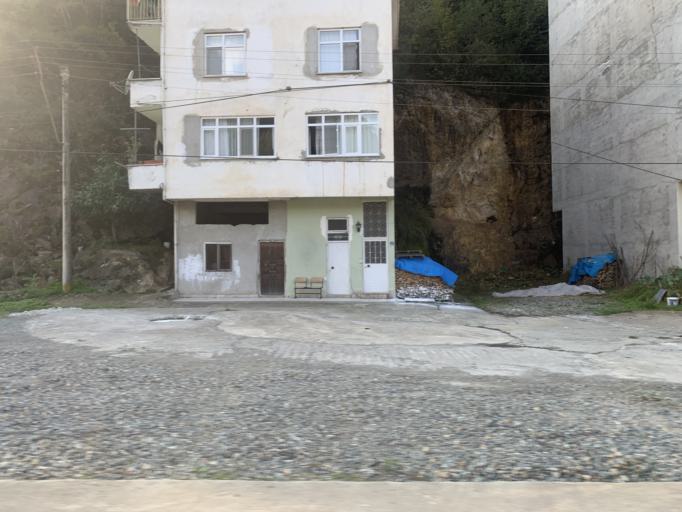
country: TR
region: Trabzon
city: Dernekpazari
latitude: 40.8295
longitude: 40.2688
